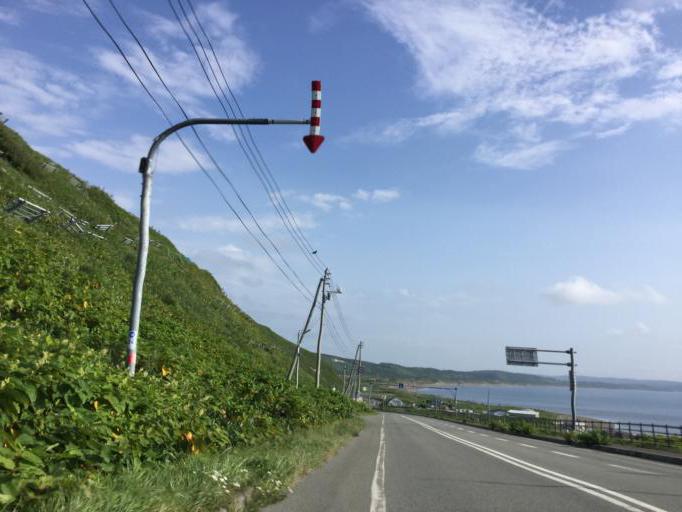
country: JP
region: Hokkaido
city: Wakkanai
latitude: 45.3777
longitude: 141.6545
